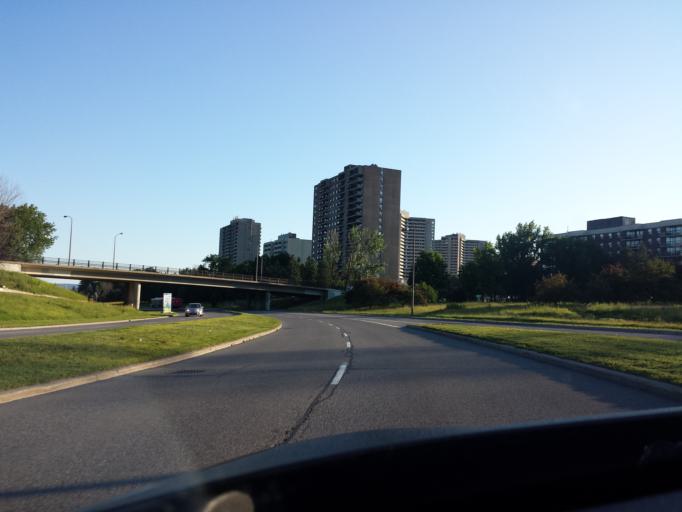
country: CA
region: Ontario
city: Bells Corners
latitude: 45.3682
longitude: -75.7829
